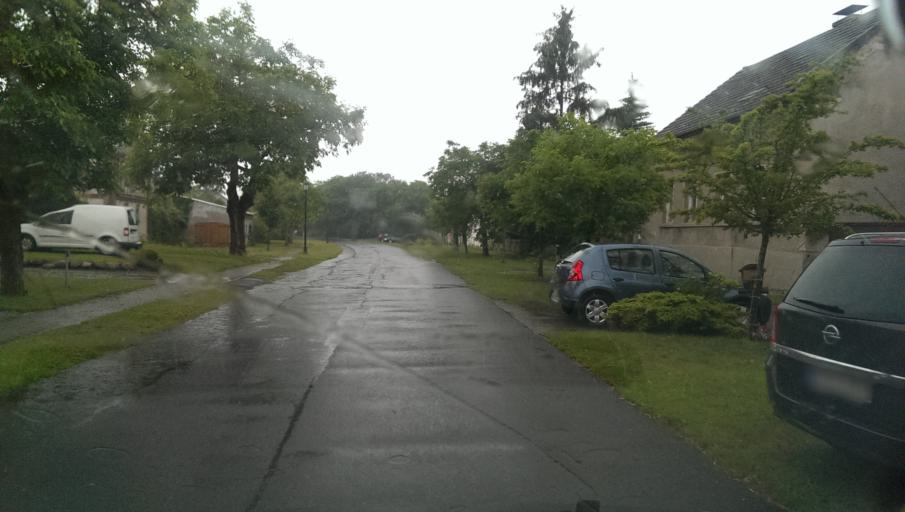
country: DE
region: Brandenburg
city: Pawesin
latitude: 52.4889
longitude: 12.6613
